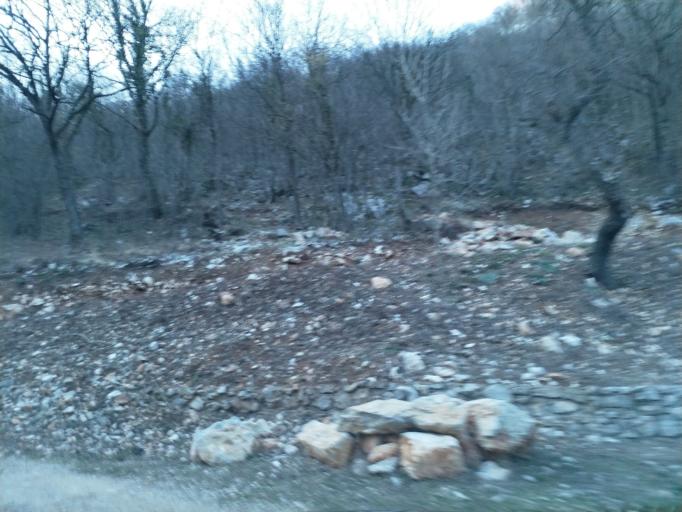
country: RS
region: Central Serbia
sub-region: Pomoravski Okrug
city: Paracin
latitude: 43.9230
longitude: 21.5278
